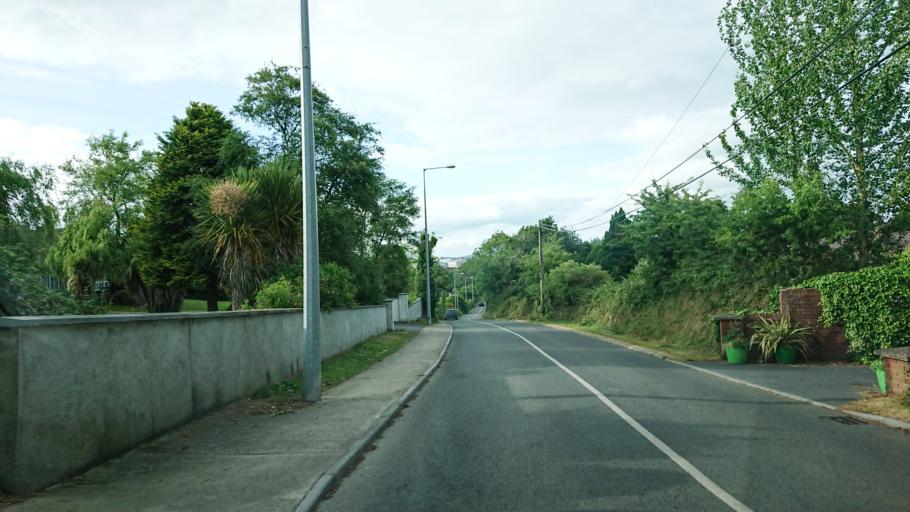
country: IE
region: Munster
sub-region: Waterford
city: Waterford
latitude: 52.2385
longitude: -7.1563
